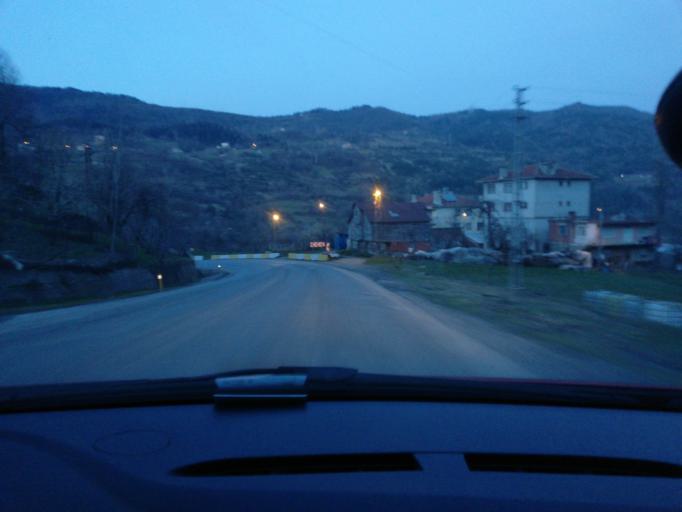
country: TR
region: Kastamonu
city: Inebolu
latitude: 41.9476
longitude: 33.7584
